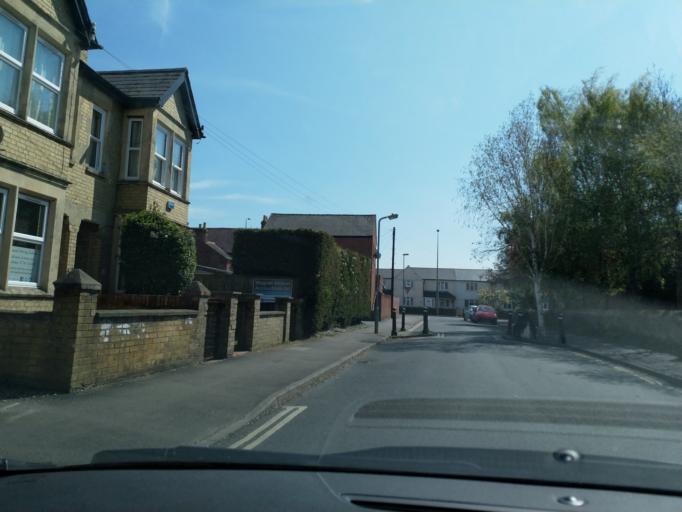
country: GB
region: England
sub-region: Oxfordshire
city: Cowley
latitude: 51.7376
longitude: -1.2087
